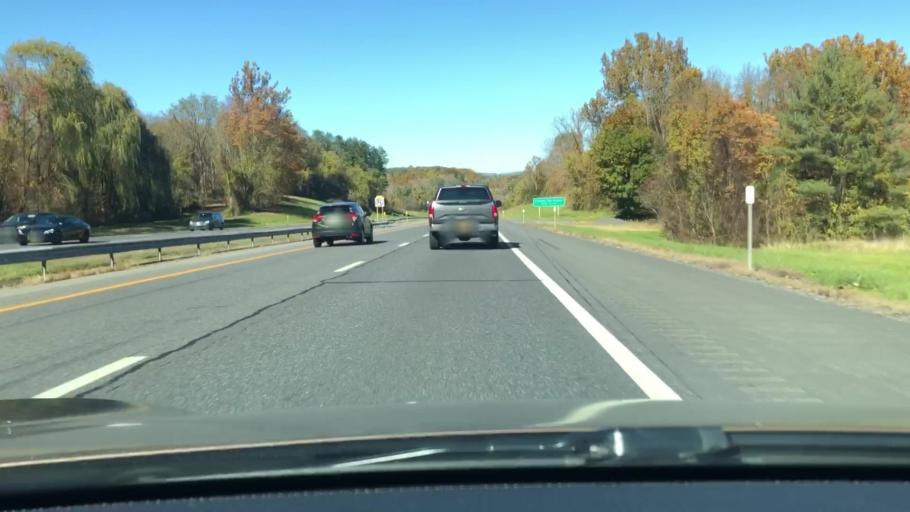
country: US
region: New York
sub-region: Ulster County
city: Rosendale Village
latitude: 41.8432
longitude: -74.0588
